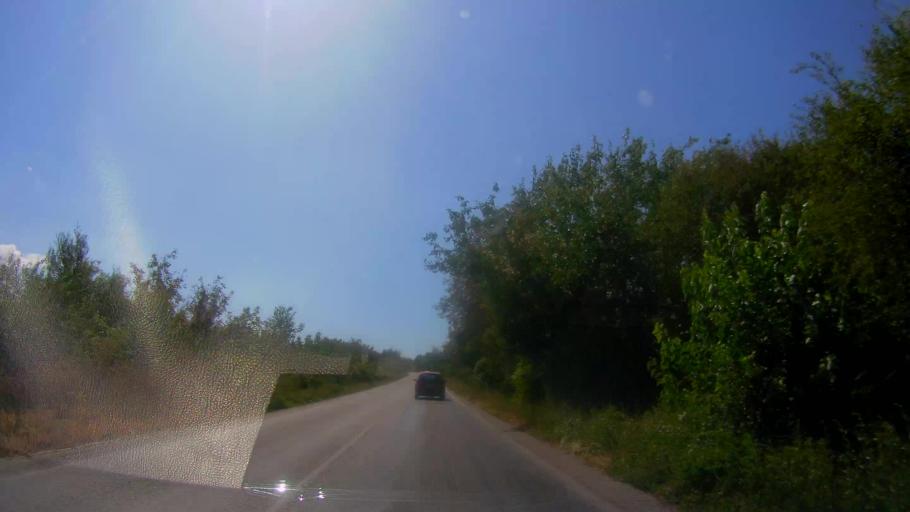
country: BG
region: Veliko Turnovo
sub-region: Obshtina Gorna Oryakhovitsa
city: Purvomaytsi
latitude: 43.2595
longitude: 25.6425
